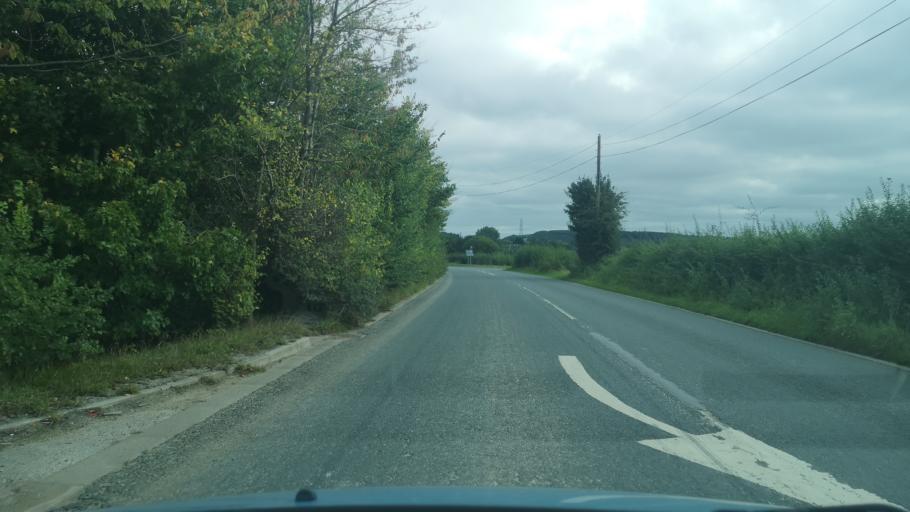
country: GB
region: England
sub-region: City and Borough of Wakefield
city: Knottingley
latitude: 53.6859
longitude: -1.2214
